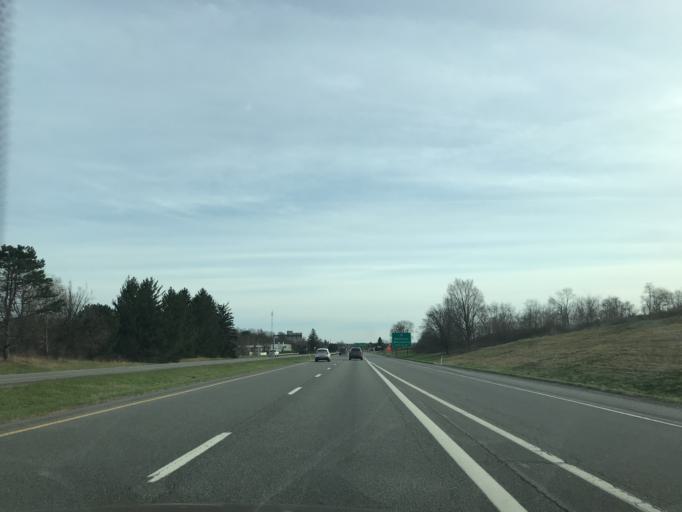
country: US
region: Pennsylvania
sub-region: Union County
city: New Columbia
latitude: 41.0593
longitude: -76.8364
